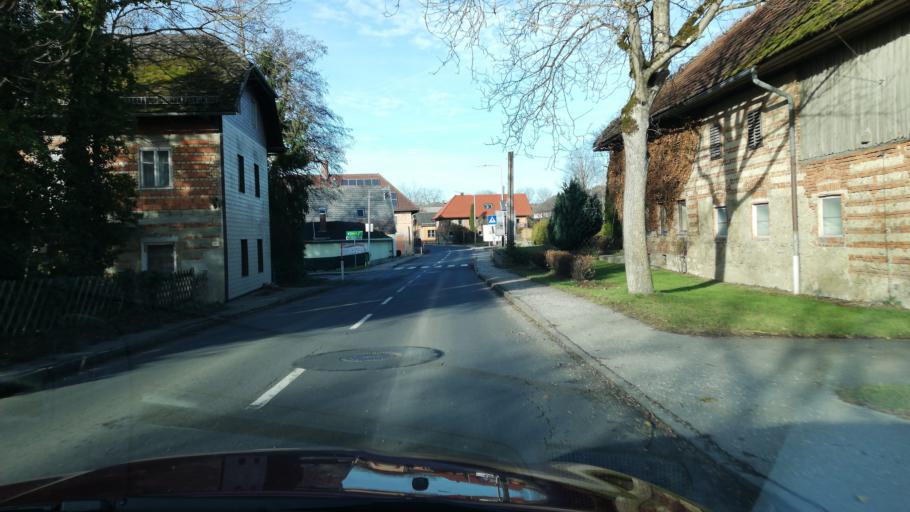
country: AT
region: Upper Austria
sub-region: Wels-Land
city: Sattledt
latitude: 48.0084
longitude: 14.0629
